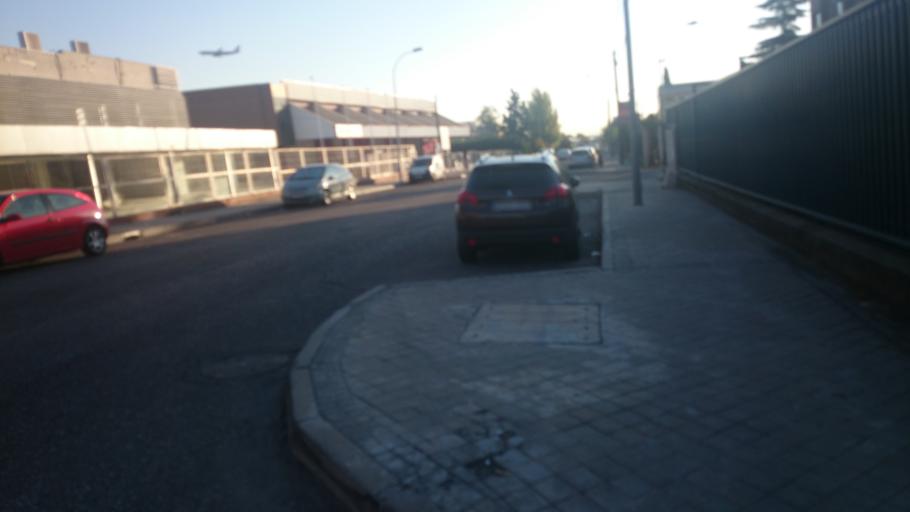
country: ES
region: Madrid
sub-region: Provincia de Madrid
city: San Fernando de Henares
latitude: 40.4369
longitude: -3.5438
